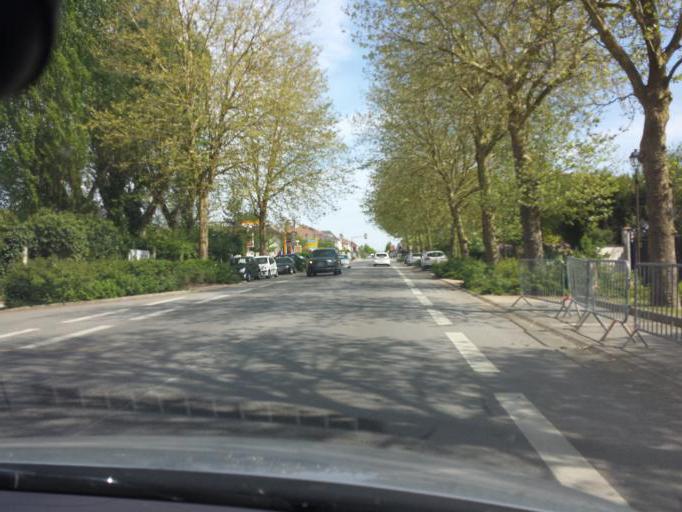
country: FR
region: Ile-de-France
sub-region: Departement des Yvelines
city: Neauphle-le-Chateau
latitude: 48.8048
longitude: 1.8945
